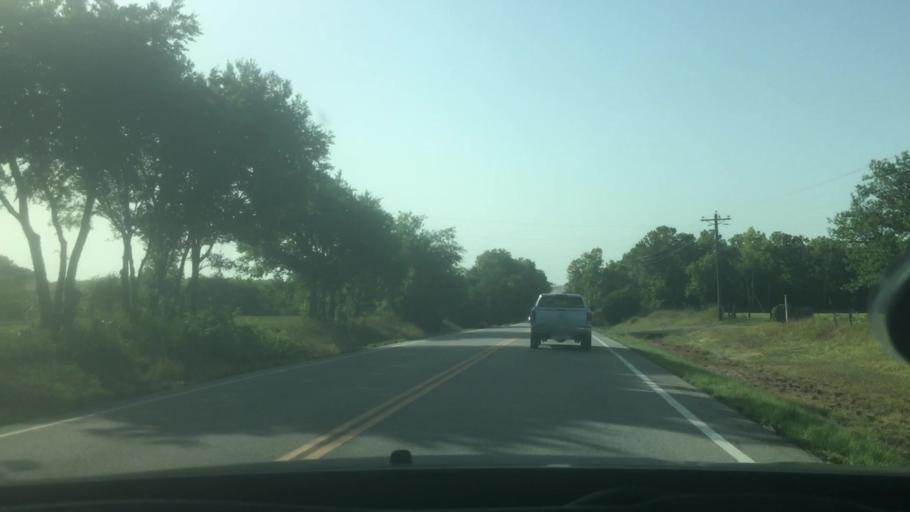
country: US
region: Oklahoma
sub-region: Bryan County
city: Durant
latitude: 34.1577
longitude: -96.3896
